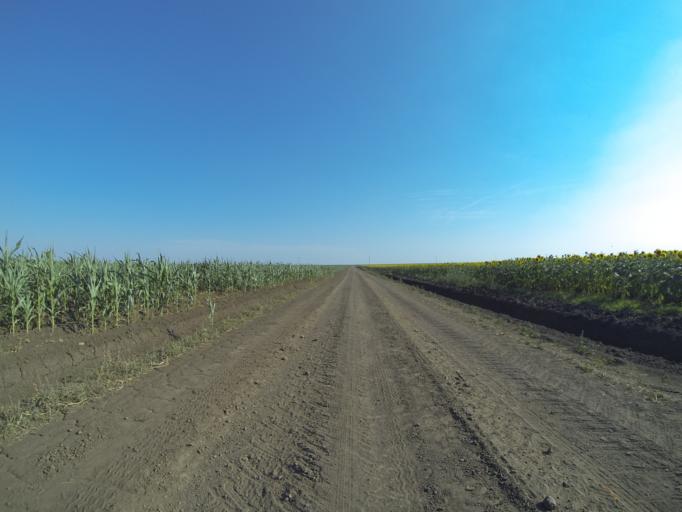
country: RO
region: Dolj
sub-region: Comuna Segarcea
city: Segarcea
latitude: 44.0703
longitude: 23.7322
